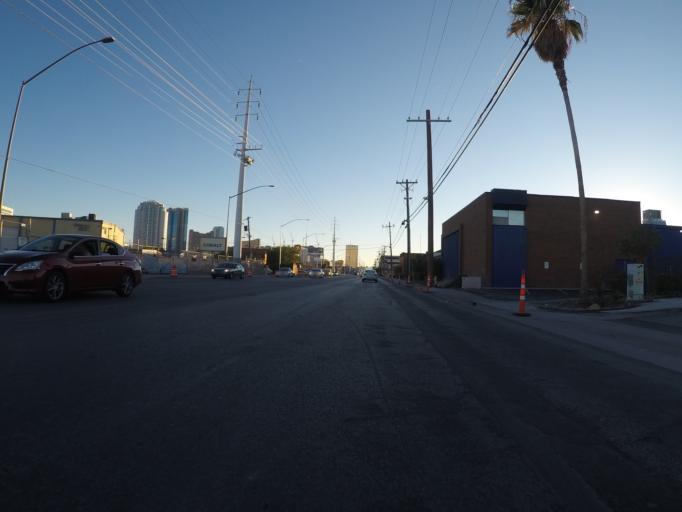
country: US
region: Nevada
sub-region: Clark County
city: Las Vegas
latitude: 36.1520
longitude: -115.1597
